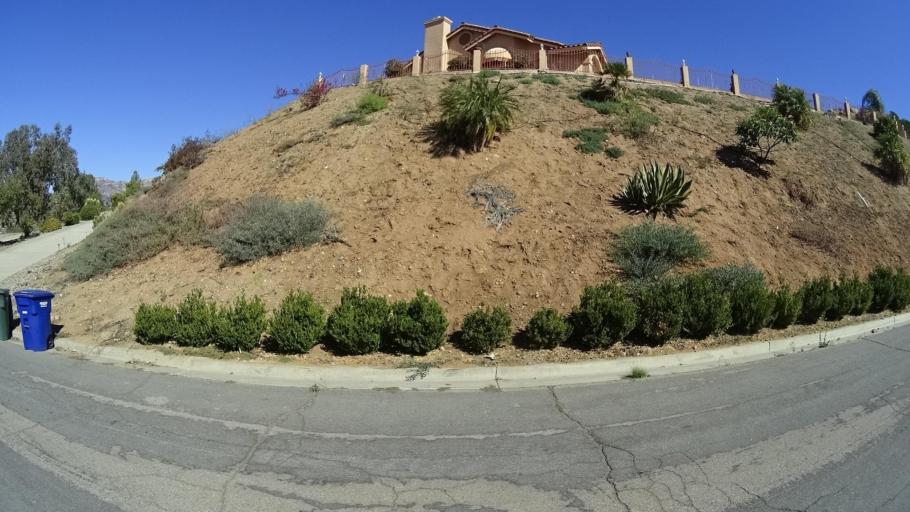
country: US
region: California
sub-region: San Diego County
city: Crest
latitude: 32.8518
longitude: -116.8624
